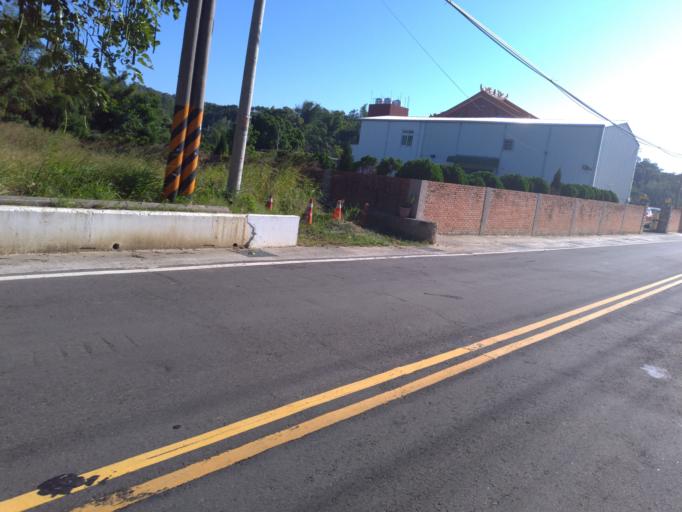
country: TW
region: Taiwan
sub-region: Hsinchu
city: Hsinchu
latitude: 24.7393
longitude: 120.9738
